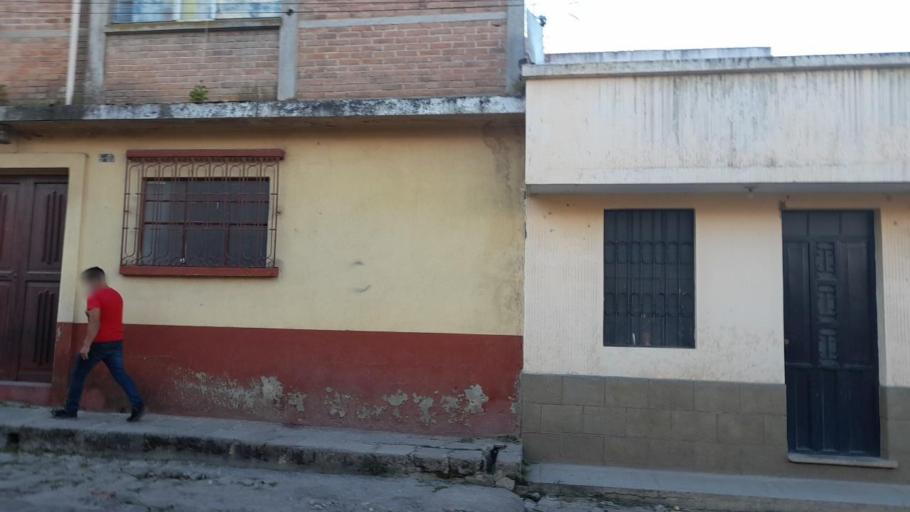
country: GT
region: Quetzaltenango
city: Quetzaltenango
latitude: 14.8307
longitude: -91.5157
